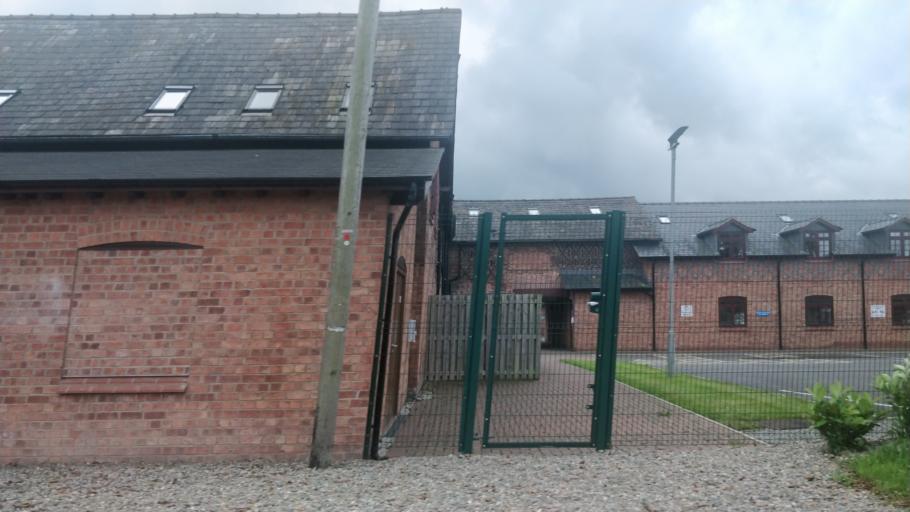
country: GB
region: England
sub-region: Cheshire West and Chester
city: Eccleston
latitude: 53.1550
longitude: -2.9270
